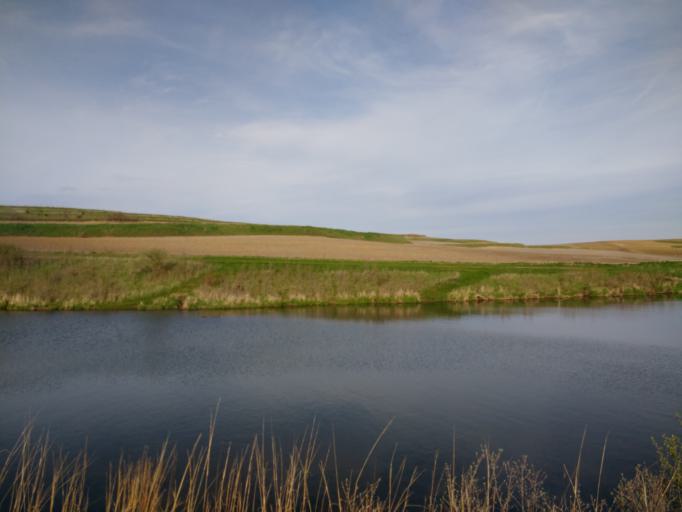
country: US
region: Iowa
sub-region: Plymouth County
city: Kingsley
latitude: 42.5983
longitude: -96.0049
